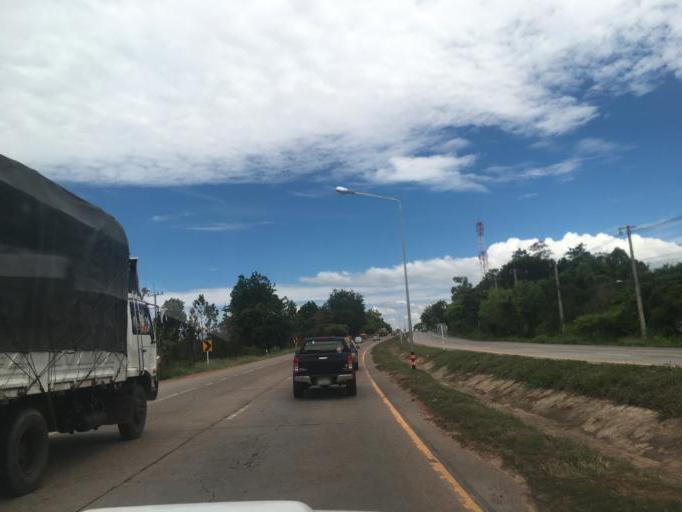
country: TH
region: Khon Kaen
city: Nam Phong
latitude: 16.6545
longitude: 102.8003
